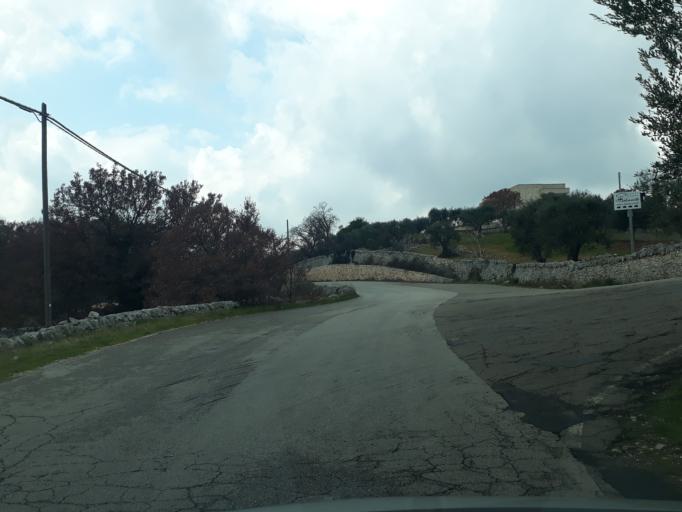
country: IT
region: Apulia
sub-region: Provincia di Brindisi
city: Lamie di Olimpie-Selva
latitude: 40.7894
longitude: 17.3278
